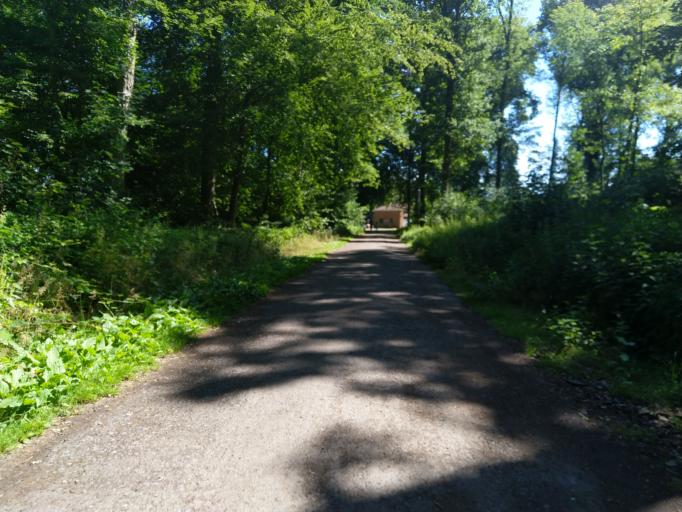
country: BE
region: Wallonia
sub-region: Province du Hainaut
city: Colfontaine
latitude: 50.3944
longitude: 3.8599
